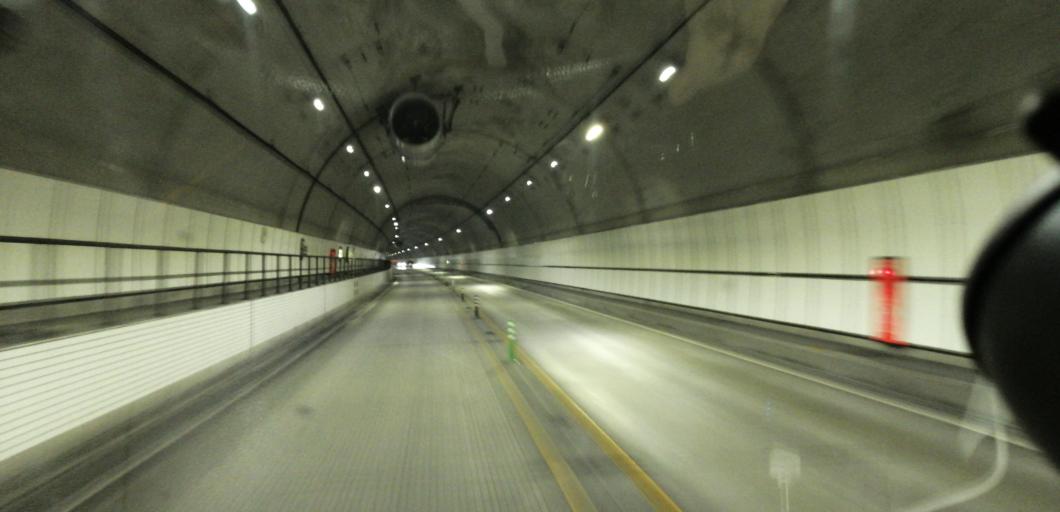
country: JP
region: Saitama
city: Yorii
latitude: 36.1002
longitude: 139.1482
